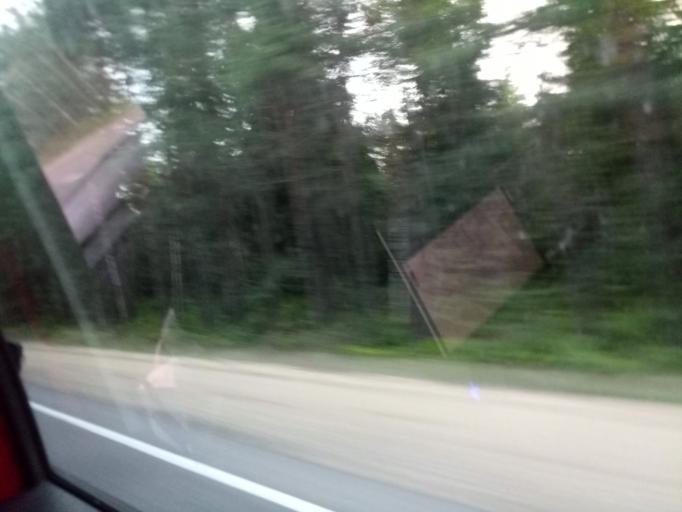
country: RU
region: Moskovskaya
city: Noginsk-9
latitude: 56.0842
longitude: 38.5772
